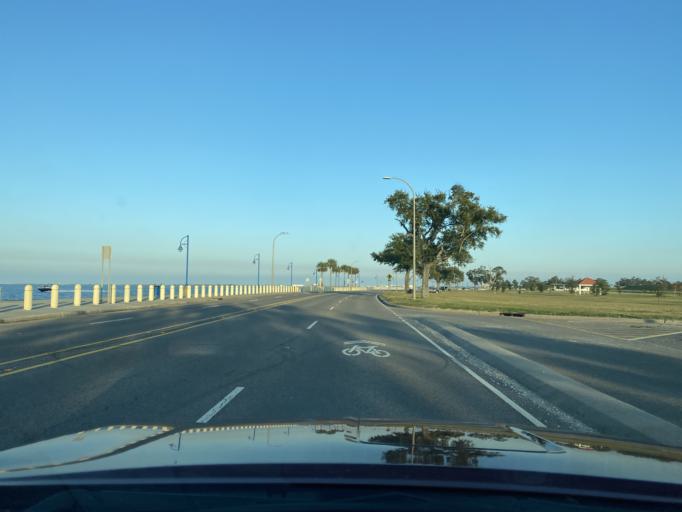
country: US
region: Louisiana
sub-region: Orleans Parish
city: New Orleans
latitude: 30.0350
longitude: -90.0479
